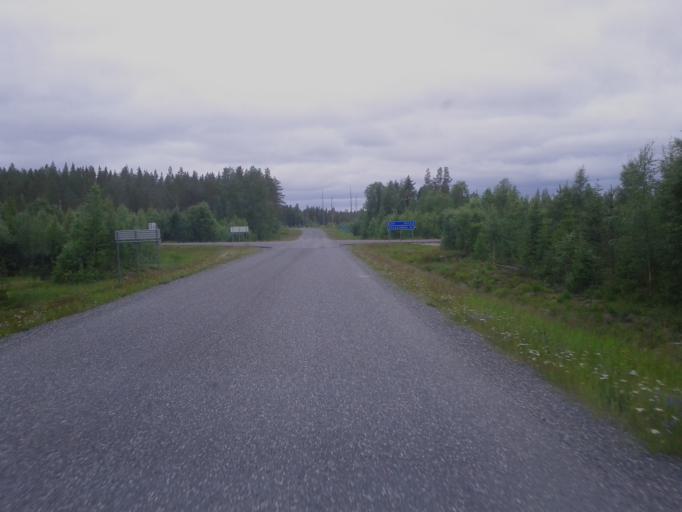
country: SE
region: Vaesterbotten
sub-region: Skelleftea Kommun
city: Storvik
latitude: 64.9877
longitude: 20.7114
